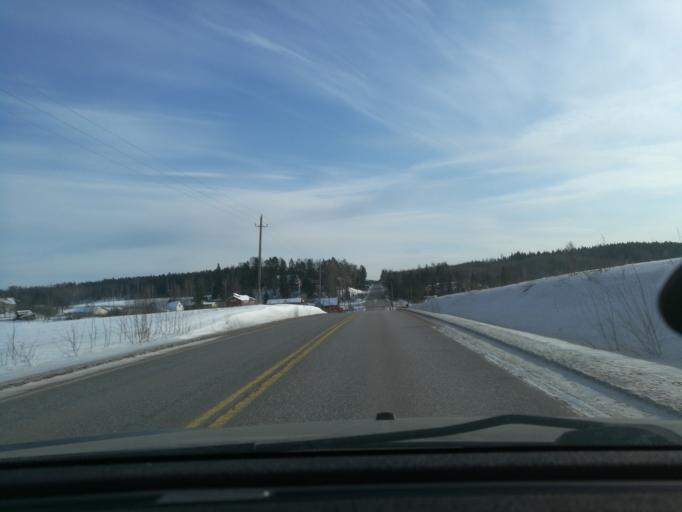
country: FI
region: Uusimaa
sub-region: Helsinki
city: Saukkola
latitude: 60.4027
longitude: 24.0626
